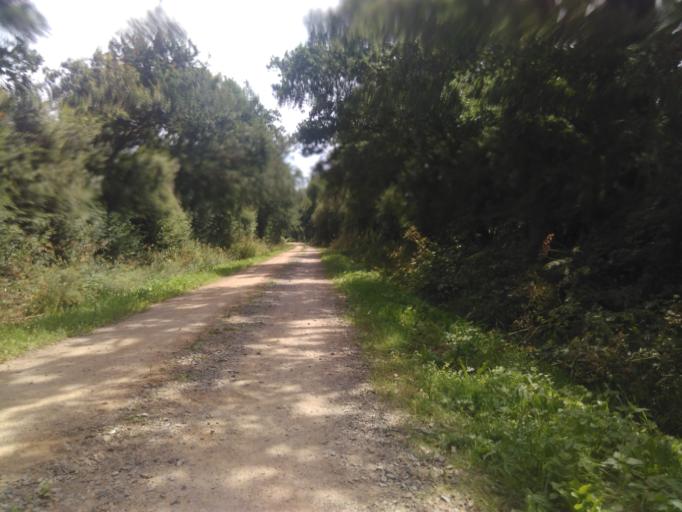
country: FR
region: Pays de la Loire
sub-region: Departement de la Vendee
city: La Ferriere
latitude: 46.7095
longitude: -1.2965
